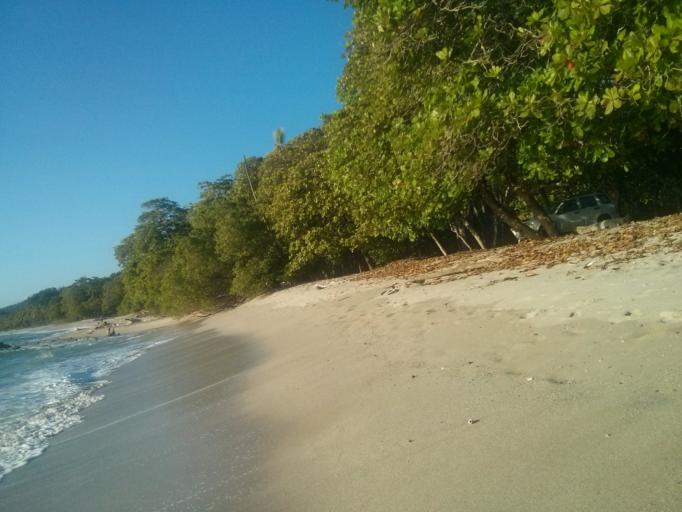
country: CR
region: Puntarenas
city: Paquera
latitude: 9.6212
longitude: -85.1478
